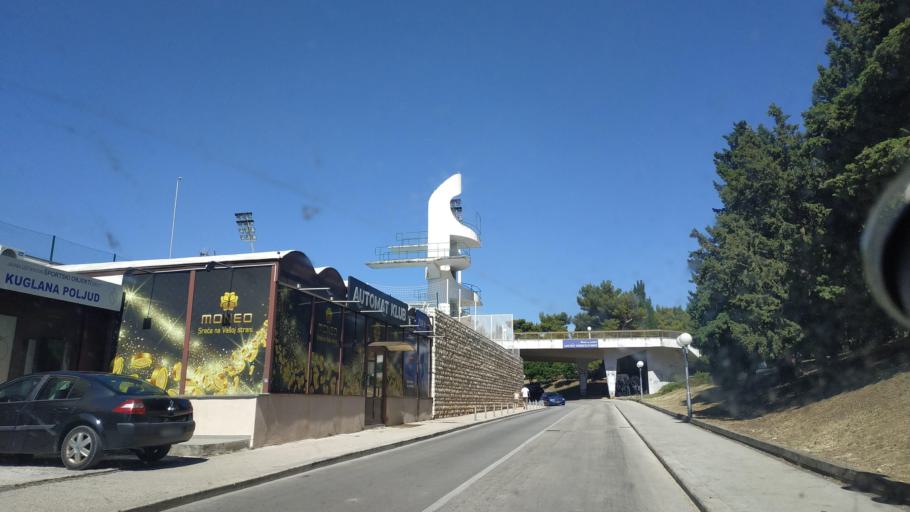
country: HR
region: Splitsko-Dalmatinska
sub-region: Grad Split
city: Split
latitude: 43.5210
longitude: 16.4314
